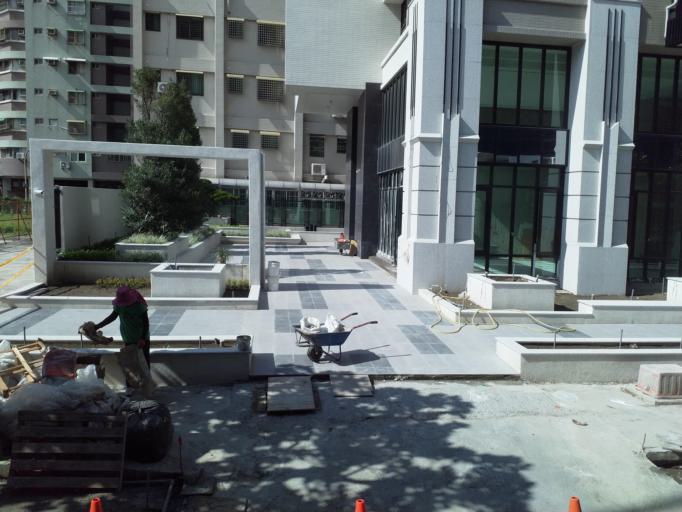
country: TW
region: Kaohsiung
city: Kaohsiung
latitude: 22.6844
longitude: 120.3064
